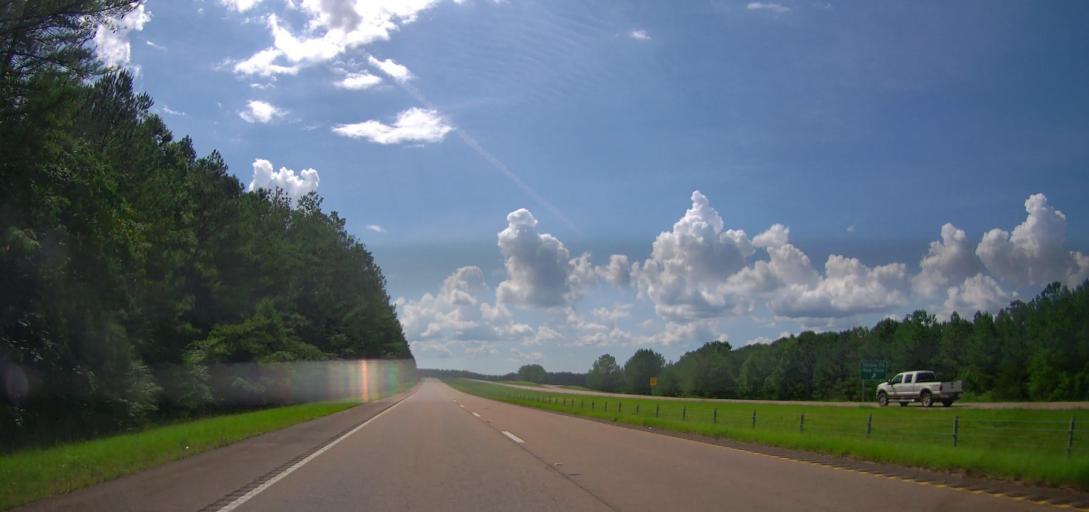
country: US
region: Mississippi
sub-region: Lowndes County
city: New Hope
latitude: 33.4962
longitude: -88.2858
